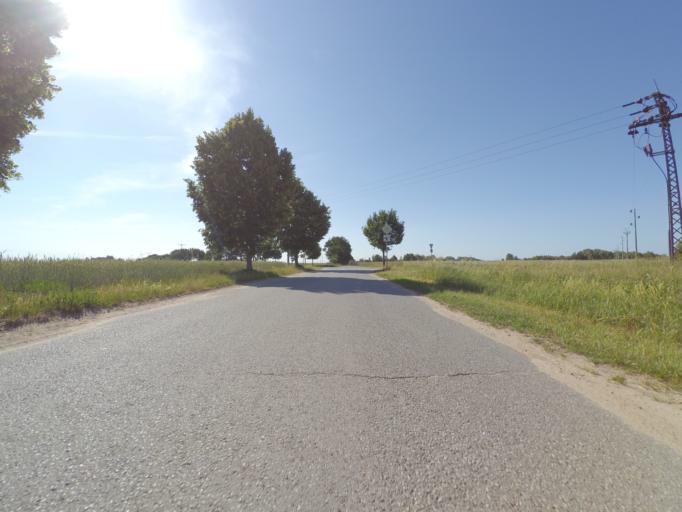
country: DE
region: Brandenburg
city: Triglitz
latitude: 53.2695
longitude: 12.0951
